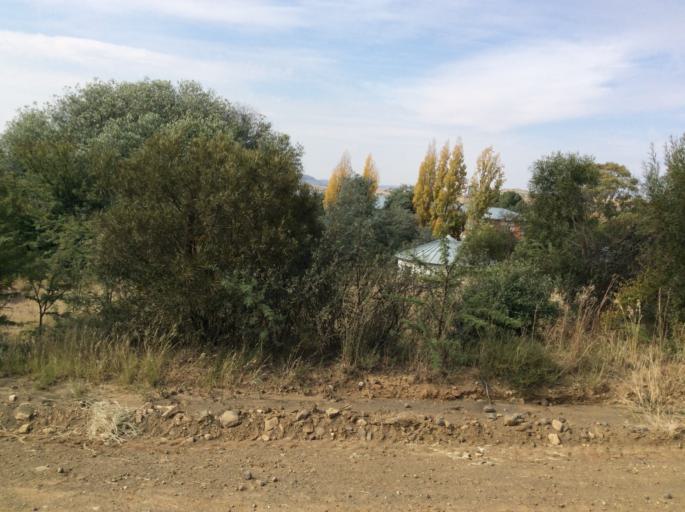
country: ZA
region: Orange Free State
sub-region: Xhariep District Municipality
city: Dewetsdorp
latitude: -29.5834
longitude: 26.6578
